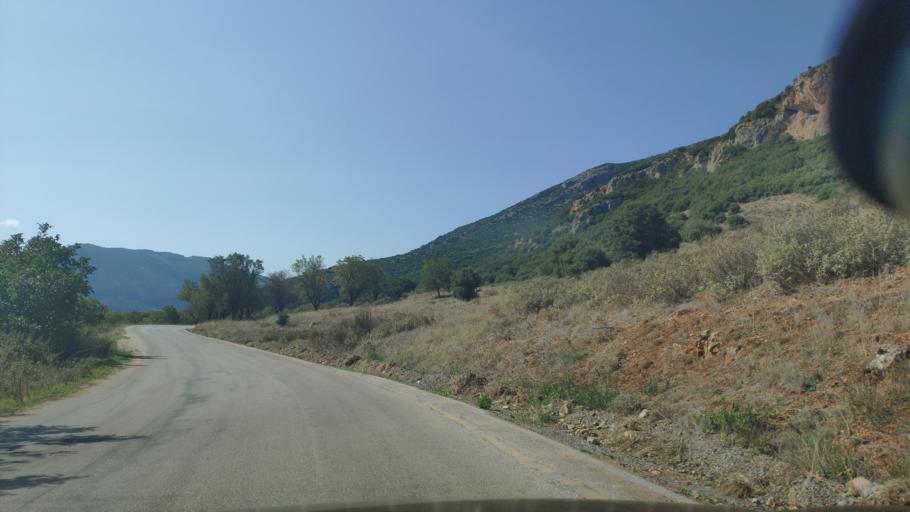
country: GR
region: Peloponnese
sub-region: Nomos Korinthias
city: Nemea
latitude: 37.9120
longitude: 22.5256
